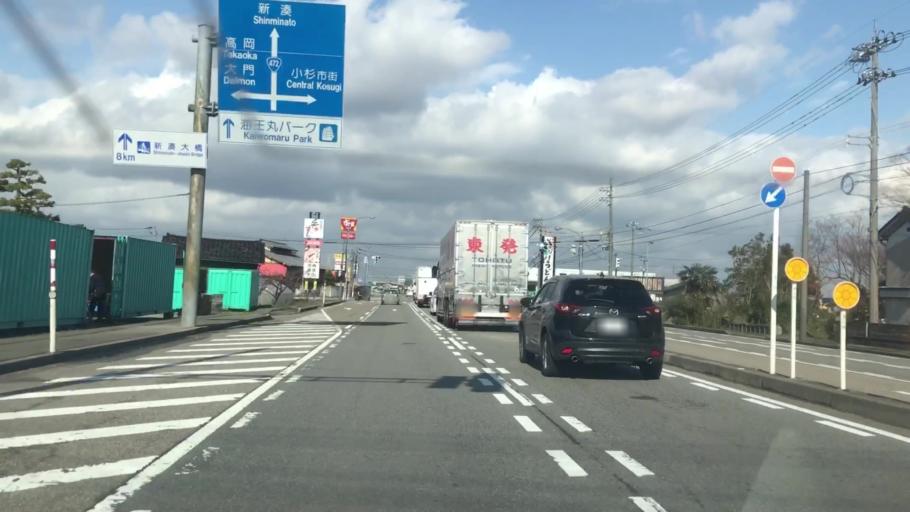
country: JP
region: Toyama
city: Kuragaki-kosugi
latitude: 36.7163
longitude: 137.0816
